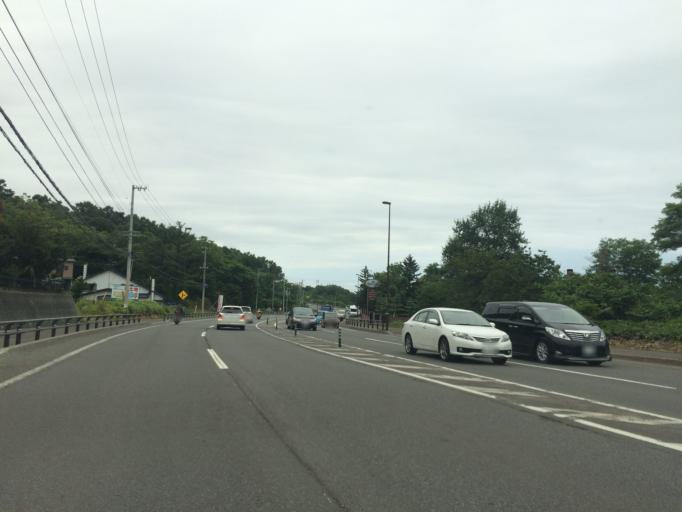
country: JP
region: Hokkaido
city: Otaru
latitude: 43.1495
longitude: 141.1342
